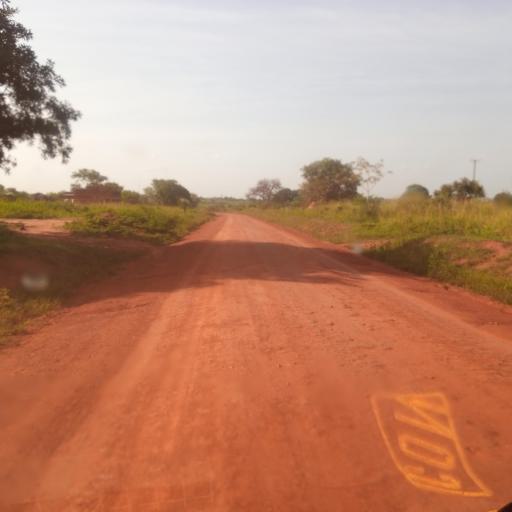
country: UG
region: Northern Region
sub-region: Kitgum District
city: Kitgum
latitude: 3.1107
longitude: 32.9146
